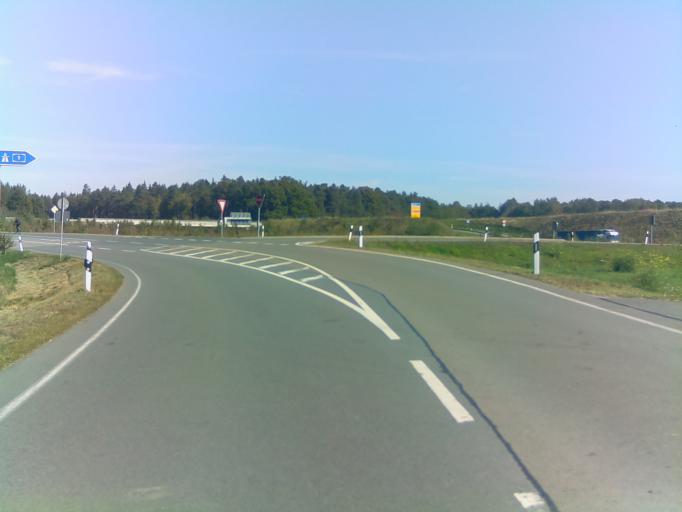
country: DE
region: Thuringia
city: Tautendorf
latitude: 50.8036
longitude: 11.8932
